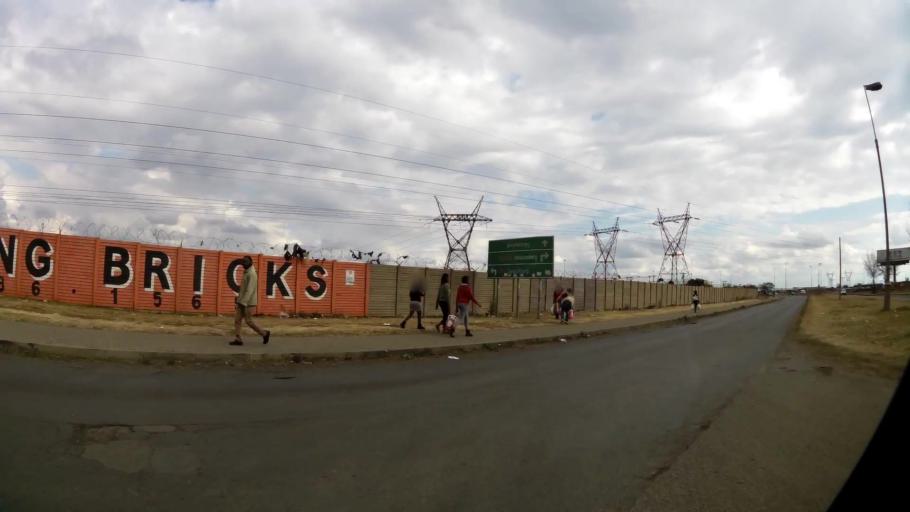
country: ZA
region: Gauteng
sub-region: Sedibeng District Municipality
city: Vanderbijlpark
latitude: -26.6901
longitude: 27.8057
